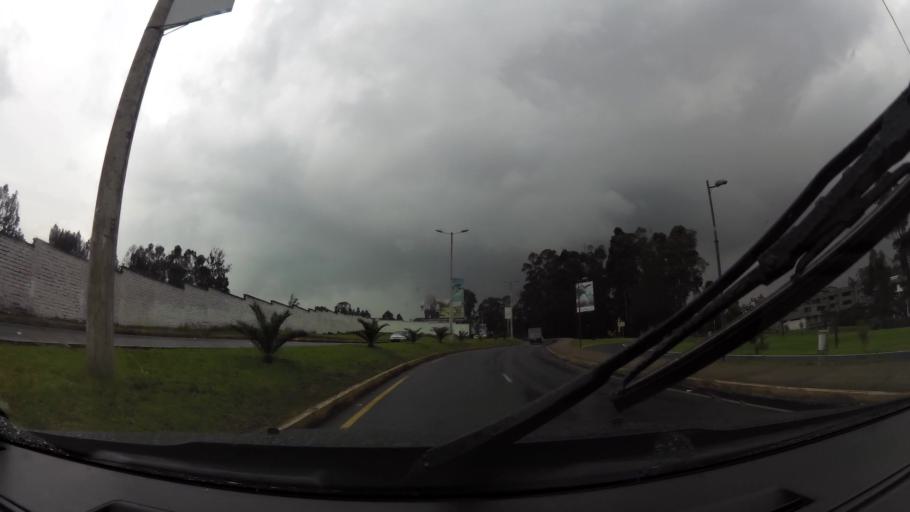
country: EC
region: Pichincha
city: Sangolqui
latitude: -0.3208
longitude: -78.4486
